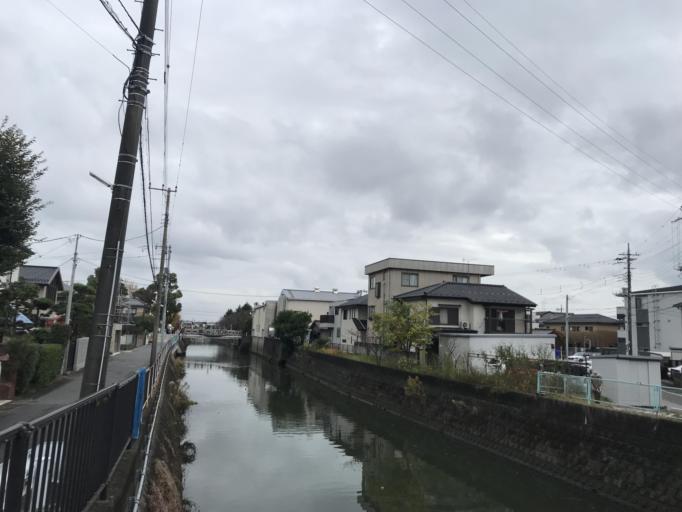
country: JP
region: Chiba
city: Matsudo
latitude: 35.7374
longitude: 139.9079
